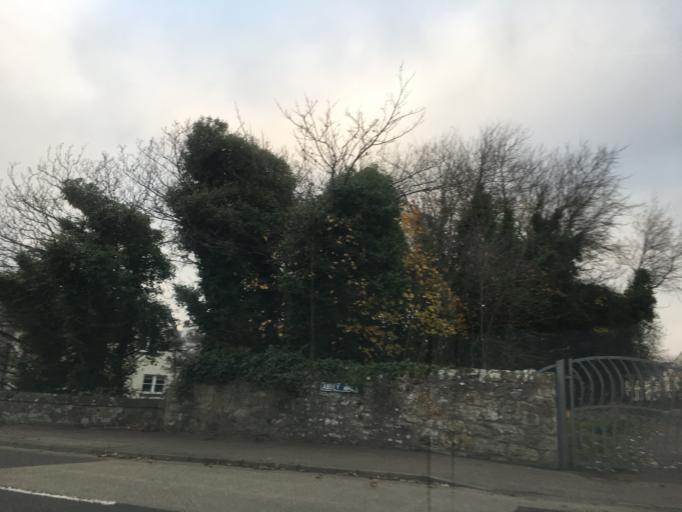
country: GB
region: Scotland
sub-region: Fife
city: Saint Andrews
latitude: 56.3365
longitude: -2.7846
